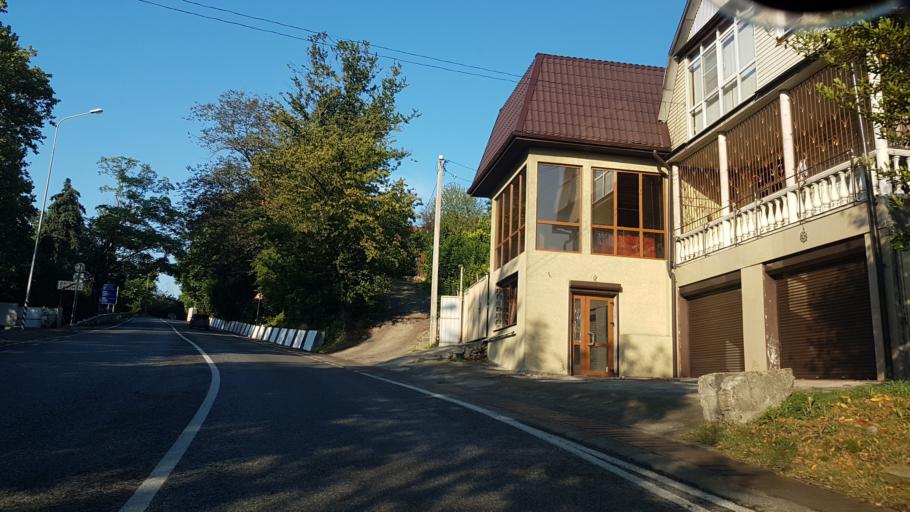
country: RU
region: Krasnodarskiy
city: Dagomys
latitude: 43.6588
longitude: 39.6502
